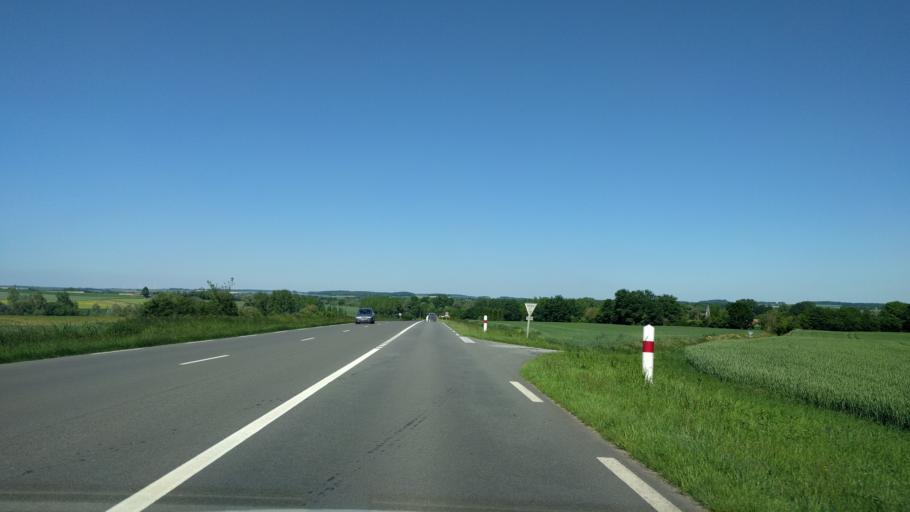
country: FR
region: Picardie
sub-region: Departement de la Somme
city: Peronne
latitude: 49.8891
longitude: 2.9146
